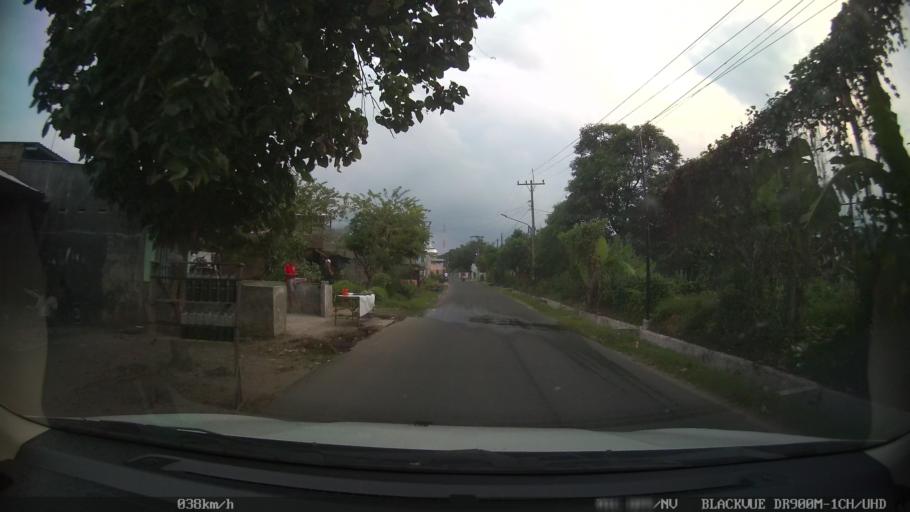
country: ID
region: North Sumatra
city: Sunggal
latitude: 3.5763
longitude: 98.6052
